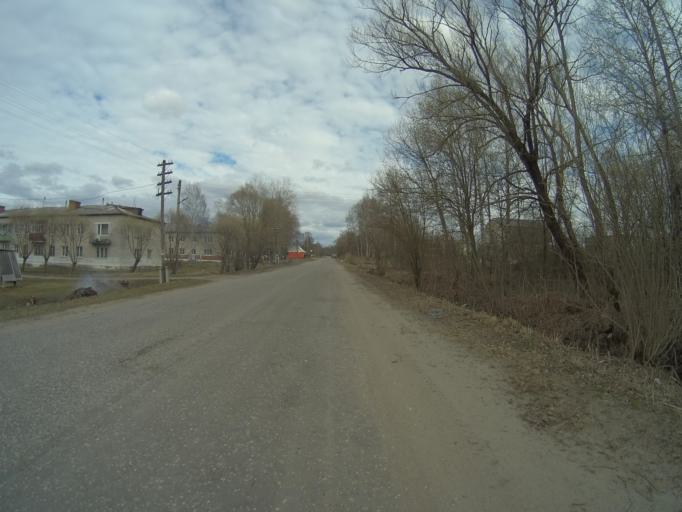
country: RU
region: Vladimir
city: Sudogda
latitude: 55.9761
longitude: 40.7308
